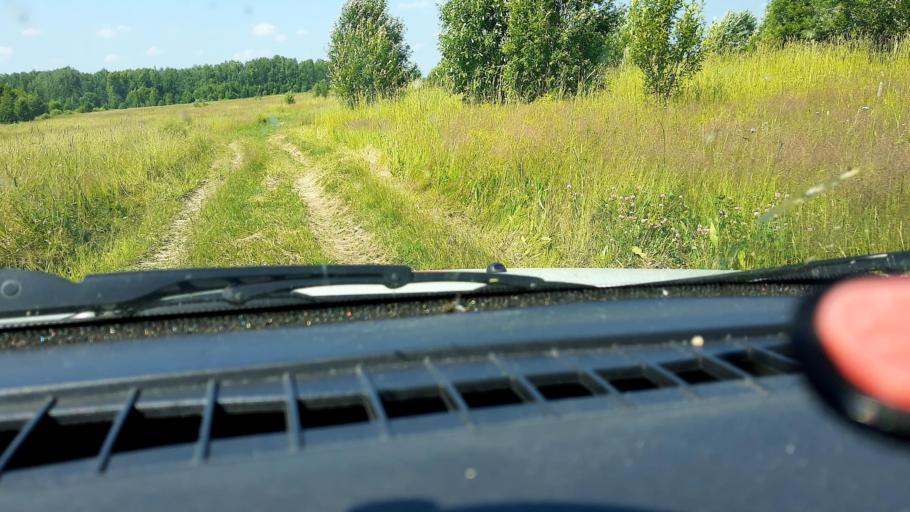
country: RU
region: Nizjnij Novgorod
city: Sharanga
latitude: 57.0458
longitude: 46.7305
